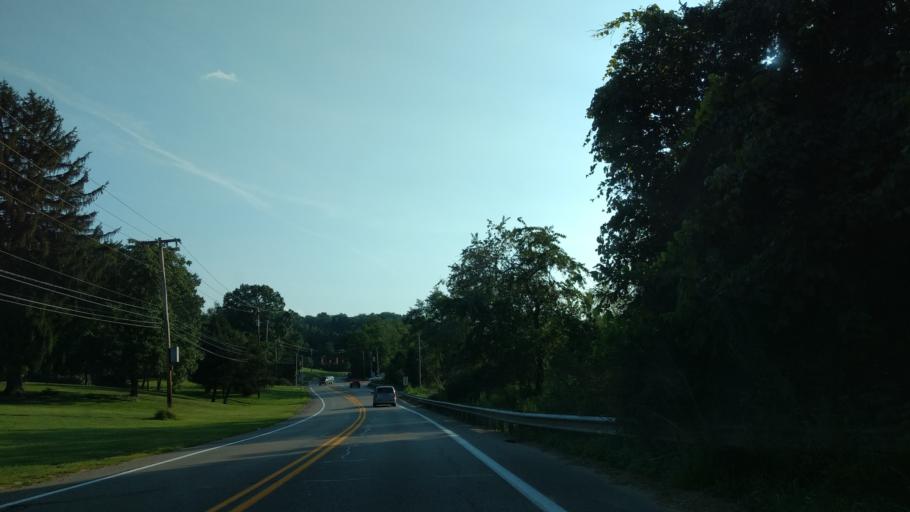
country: US
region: Pennsylvania
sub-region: Allegheny County
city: Gibsonia
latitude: 40.5882
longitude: -80.0212
